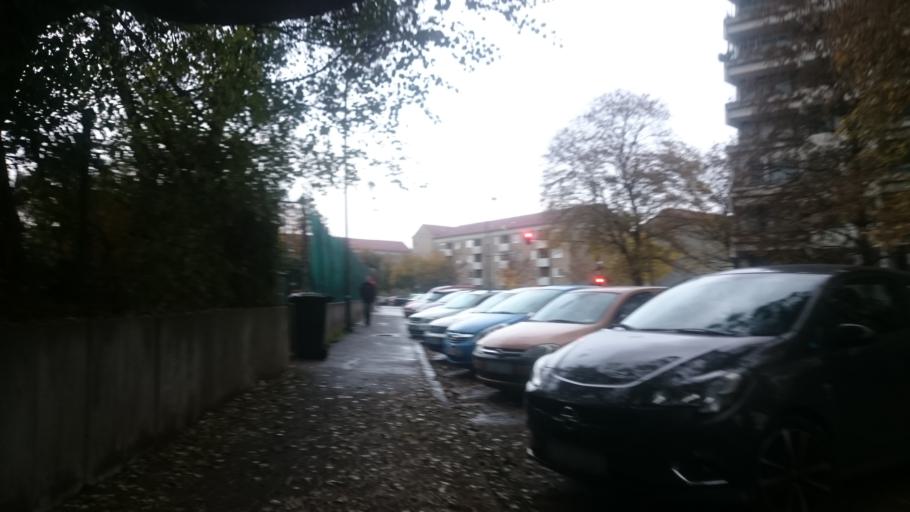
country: DE
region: Bavaria
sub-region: Swabia
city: Augsburg
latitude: 48.3570
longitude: 10.9223
